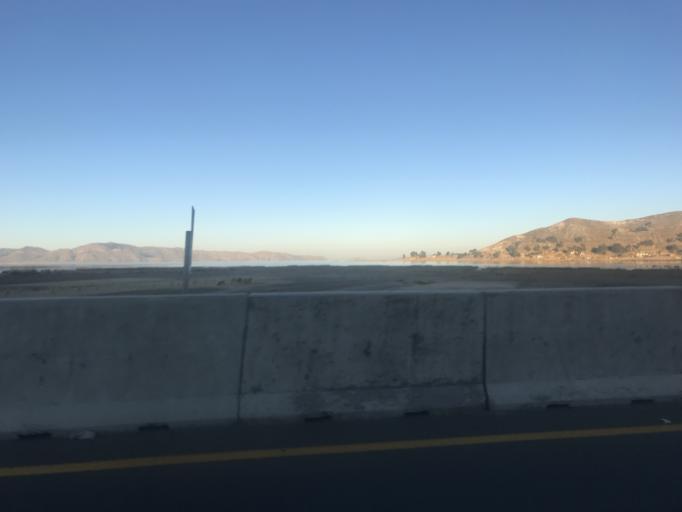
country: BO
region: La Paz
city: Huarina
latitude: -16.2405
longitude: -68.5753
